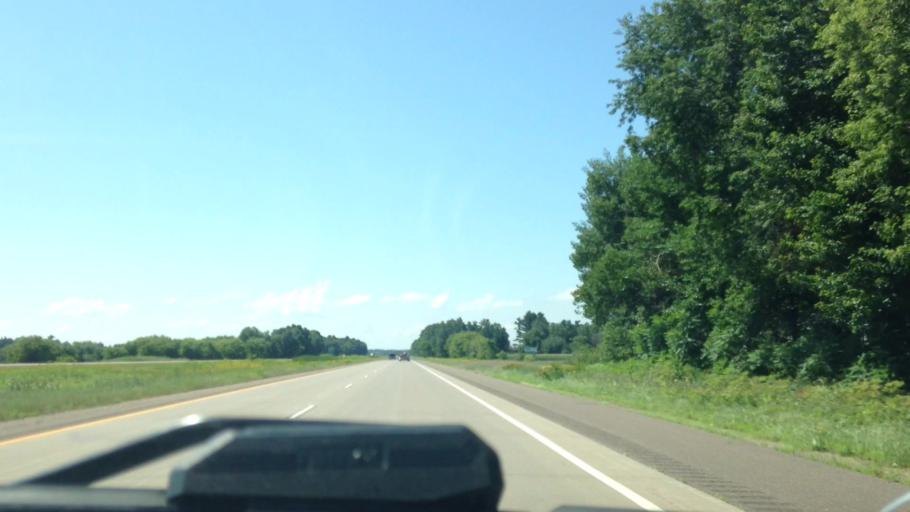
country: US
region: Wisconsin
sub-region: Barron County
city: Cameron
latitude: 45.4382
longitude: -91.7607
